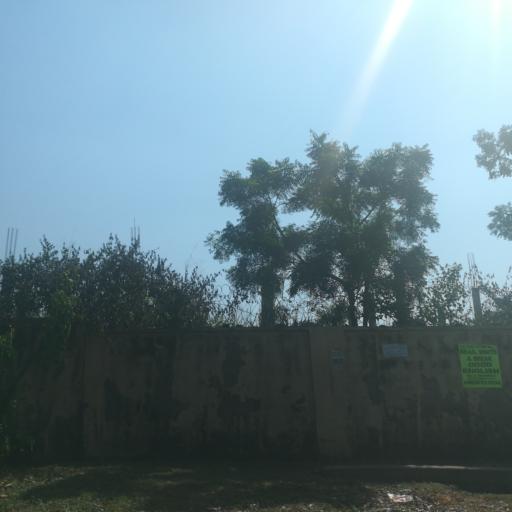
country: NG
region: Abuja Federal Capital Territory
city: Abuja
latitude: 9.0700
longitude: 7.4465
